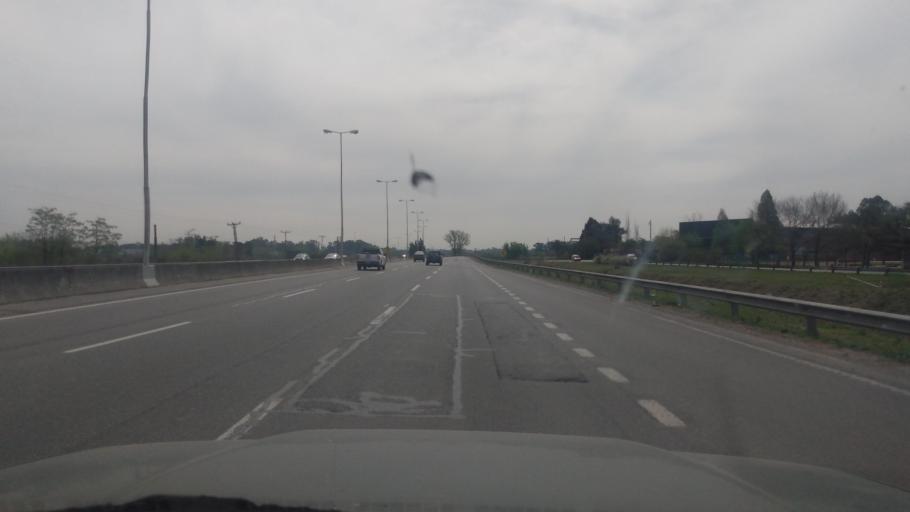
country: AR
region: Buenos Aires
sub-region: Partido de Pilar
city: Pilar
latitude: -34.4160
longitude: -59.0035
